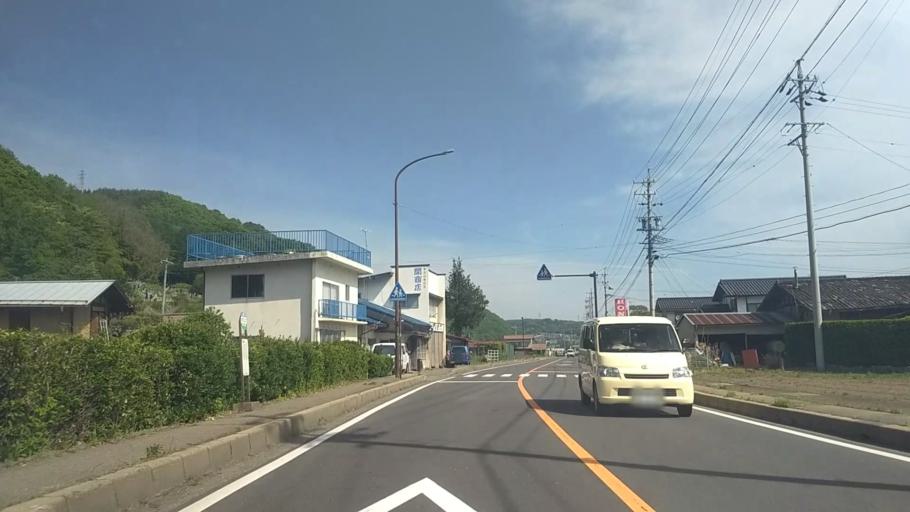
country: JP
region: Nagano
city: Saku
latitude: 36.1129
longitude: 138.4738
